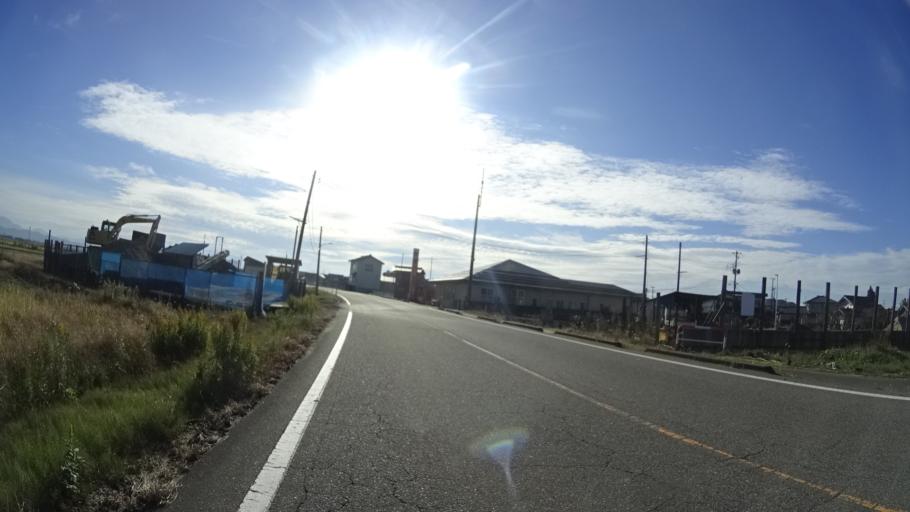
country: JP
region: Niigata
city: Mitsuke
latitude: 37.5770
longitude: 138.8356
